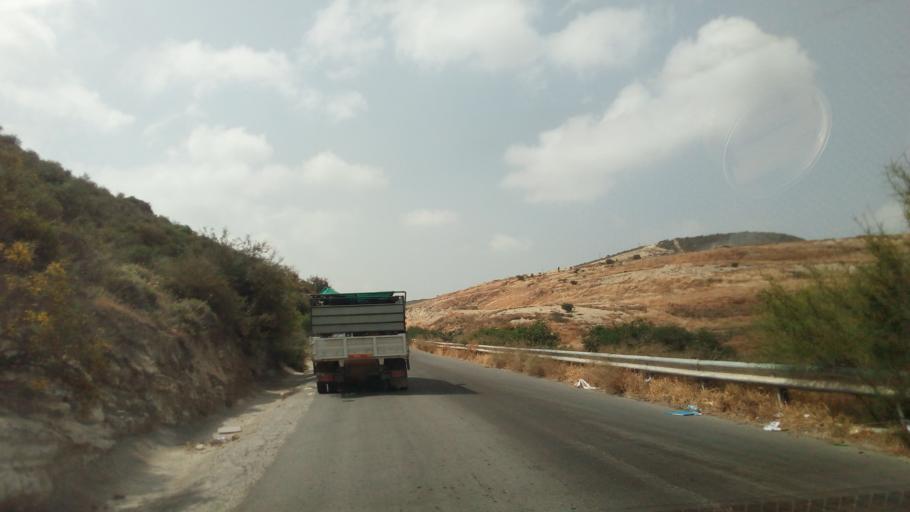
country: CY
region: Limassol
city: Pano Polemidia
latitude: 34.7525
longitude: 32.9538
